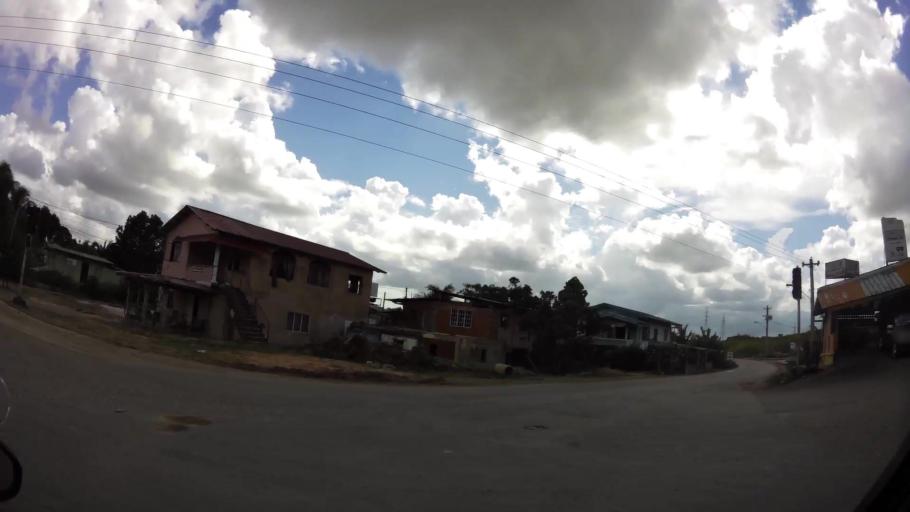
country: TT
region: Penal/Debe
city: Debe
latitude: 10.2223
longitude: -61.4419
